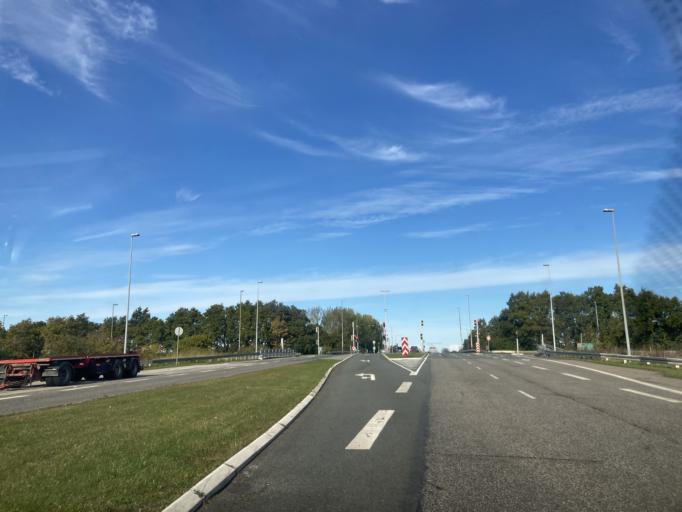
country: DK
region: Capital Region
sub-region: Vallensbaek Kommune
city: Vallensbaek
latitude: 55.6413
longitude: 12.3726
